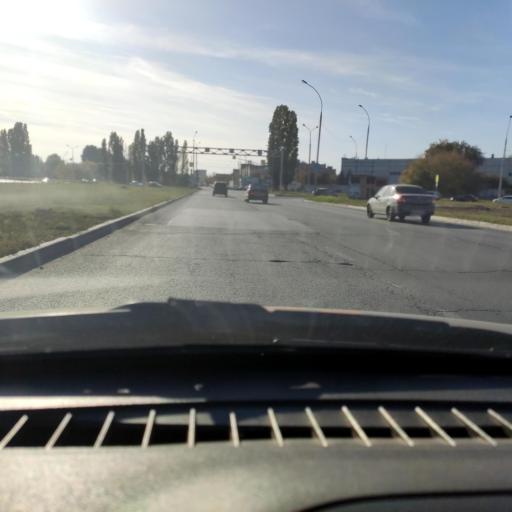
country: RU
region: Samara
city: Tol'yatti
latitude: 53.5433
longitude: 49.3174
